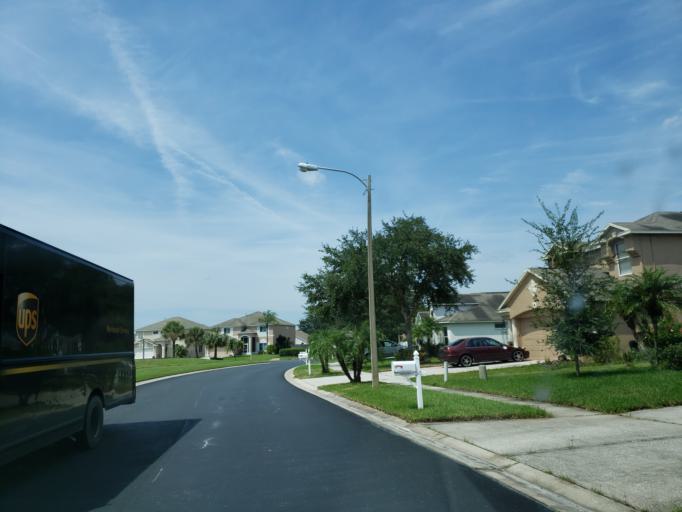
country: US
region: Florida
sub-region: Pasco County
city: Wesley Chapel
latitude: 28.2258
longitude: -82.3877
